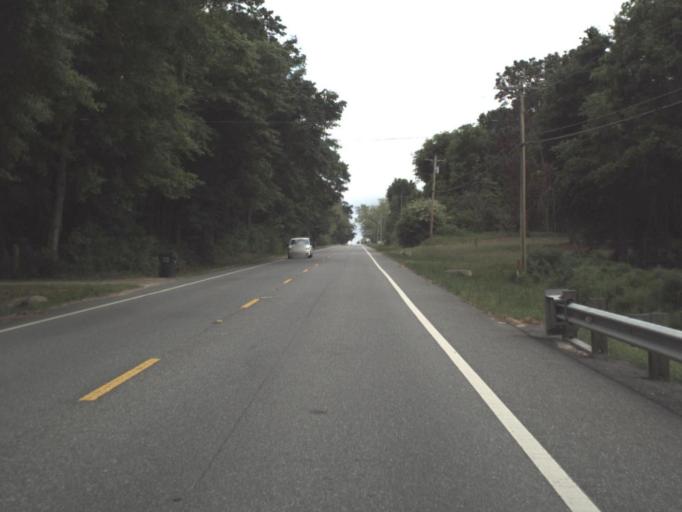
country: US
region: Florida
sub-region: Santa Rosa County
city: Point Baker
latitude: 30.8417
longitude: -87.0507
